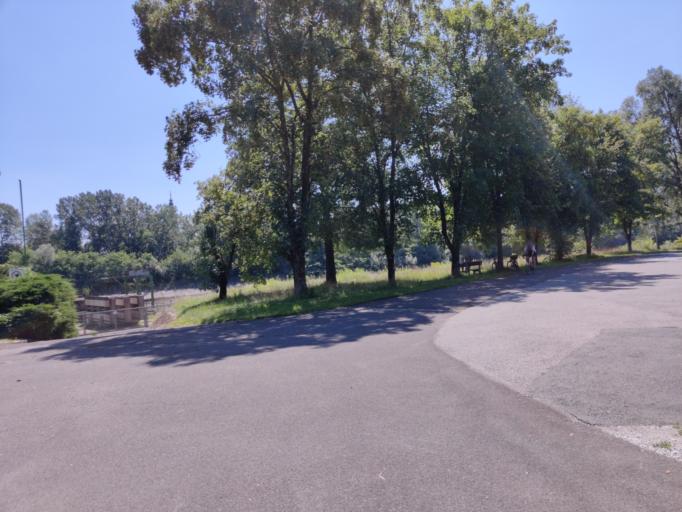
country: AT
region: Styria
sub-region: Politischer Bezirk Leibnitz
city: Gabersdorf
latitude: 46.7852
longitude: 15.5842
